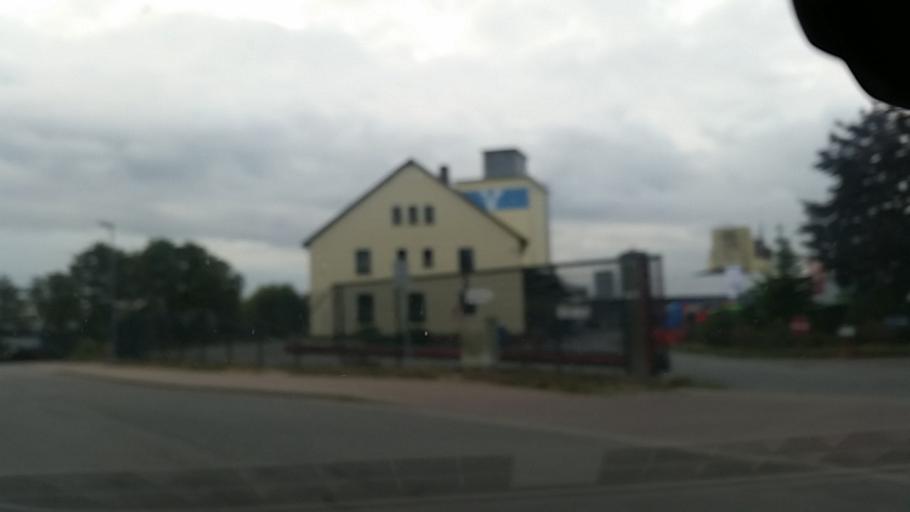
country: DE
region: Lower Saxony
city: Hankensbuttel
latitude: 52.7252
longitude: 10.6100
